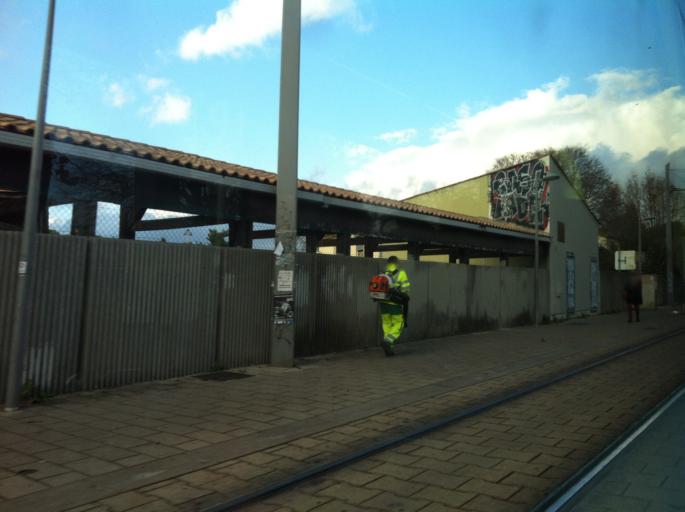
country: FR
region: Languedoc-Roussillon
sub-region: Departement de l'Herault
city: Montpellier
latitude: 43.6272
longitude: 3.8653
